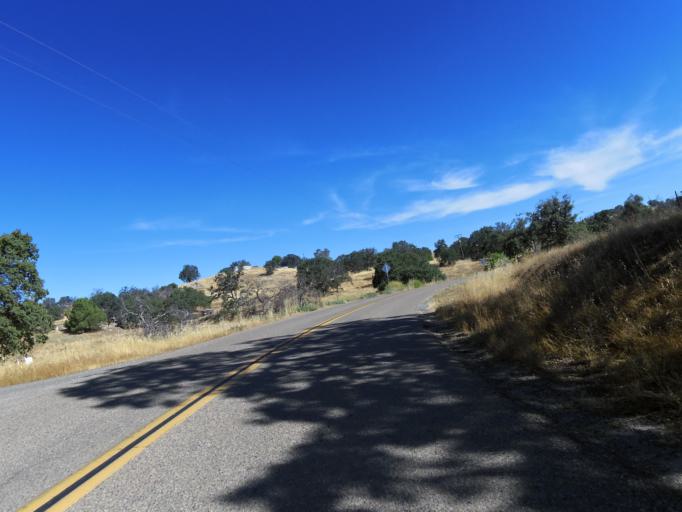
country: US
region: California
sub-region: Madera County
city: Yosemite Lakes
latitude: 37.2197
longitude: -119.9073
